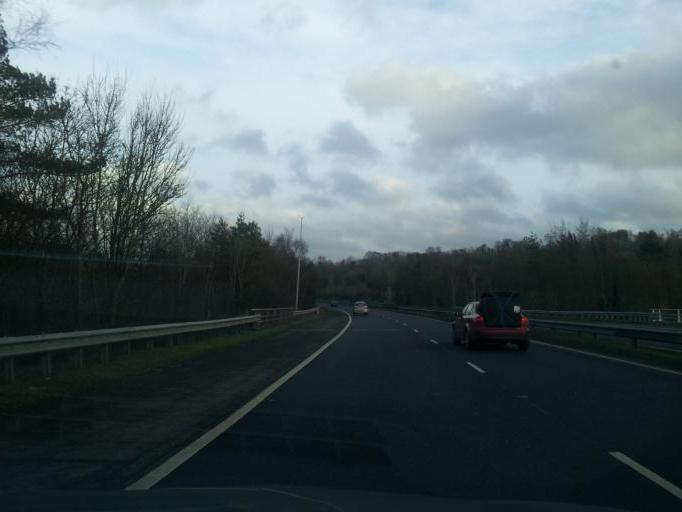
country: GB
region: England
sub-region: Hertfordshire
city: Tring
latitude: 51.7870
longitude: -0.6760
